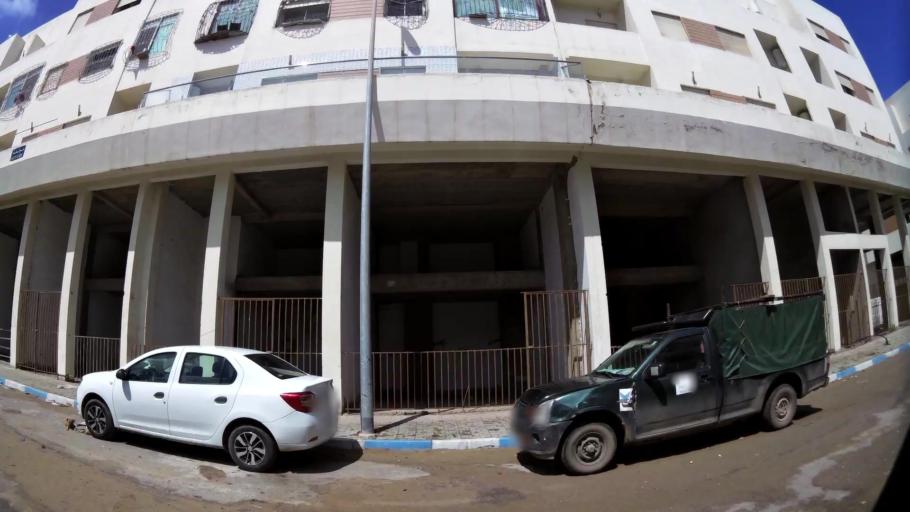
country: MA
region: Grand Casablanca
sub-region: Mohammedia
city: Mohammedia
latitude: 33.6401
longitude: -7.4476
